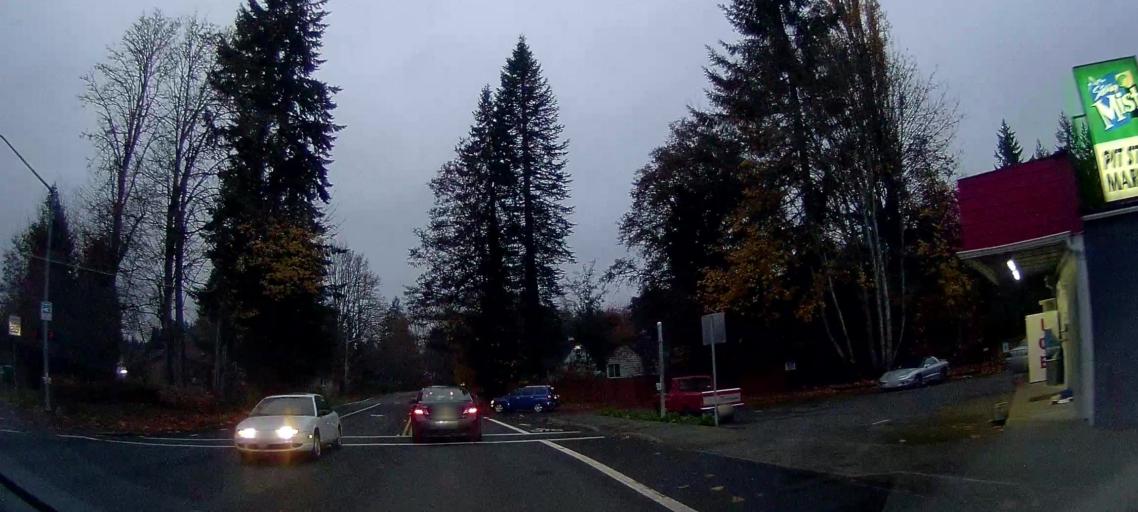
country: US
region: Washington
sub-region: Thurston County
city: Olympia
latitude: 47.0327
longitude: -122.8660
